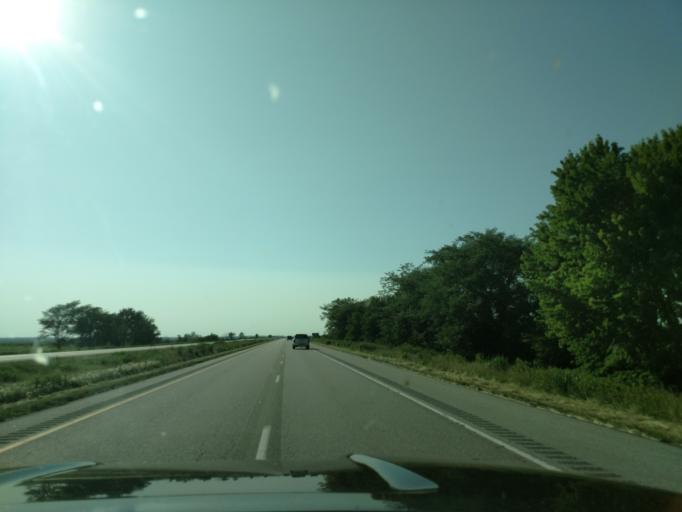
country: US
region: Iowa
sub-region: Fremont County
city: Hamburg
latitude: 40.5912
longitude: -95.6655
